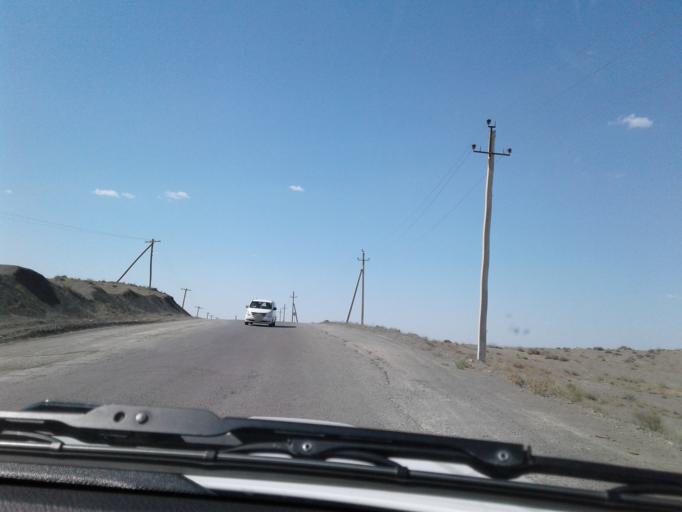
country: TM
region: Balkan
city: Magtymguly
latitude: 38.4989
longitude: 56.1933
